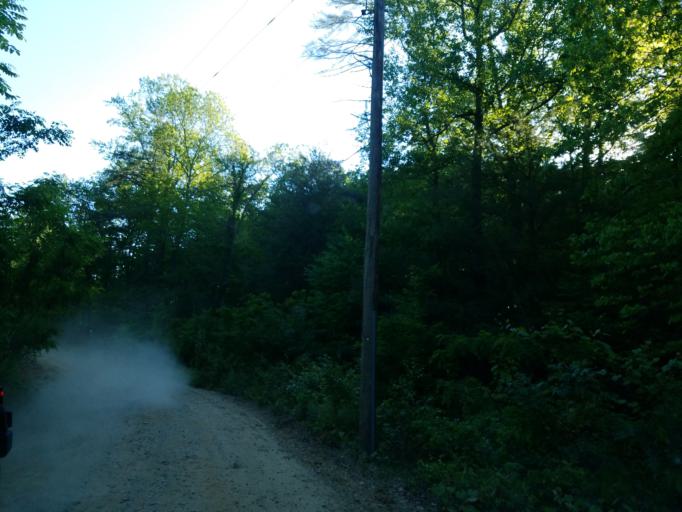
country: US
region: Georgia
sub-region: Fannin County
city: Blue Ridge
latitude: 34.7155
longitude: -84.1566
